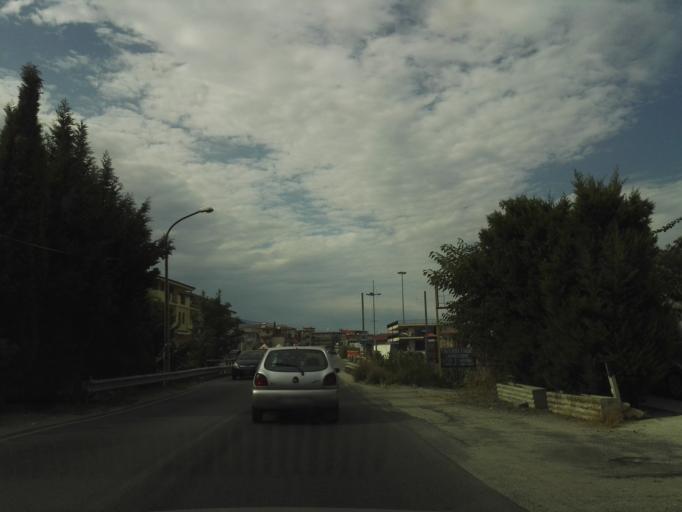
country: IT
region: Calabria
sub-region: Provincia di Catanzaro
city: Marina di Davoli
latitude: 38.6609
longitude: 16.5449
